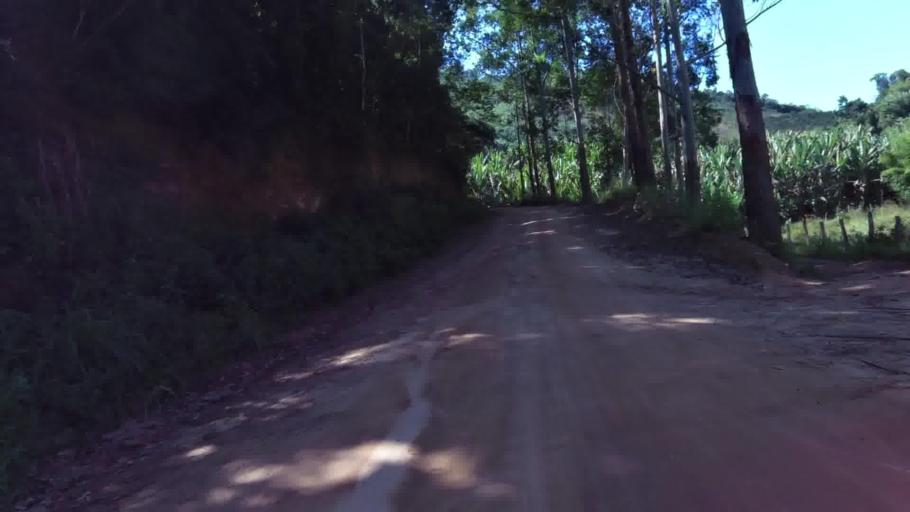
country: BR
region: Espirito Santo
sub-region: Alfredo Chaves
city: Alfredo Chaves
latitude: -20.5713
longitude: -40.7857
